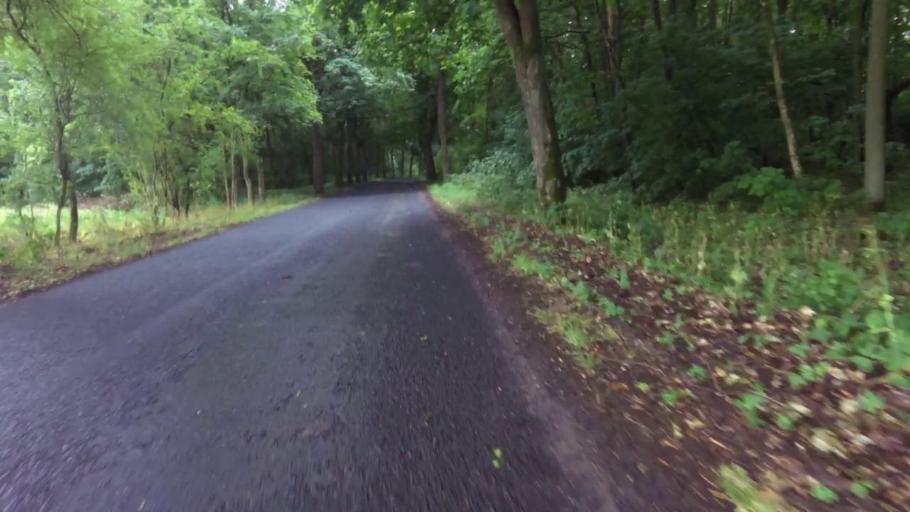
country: PL
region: West Pomeranian Voivodeship
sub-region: Powiat choszczenski
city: Choszczno
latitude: 53.2224
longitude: 15.3803
